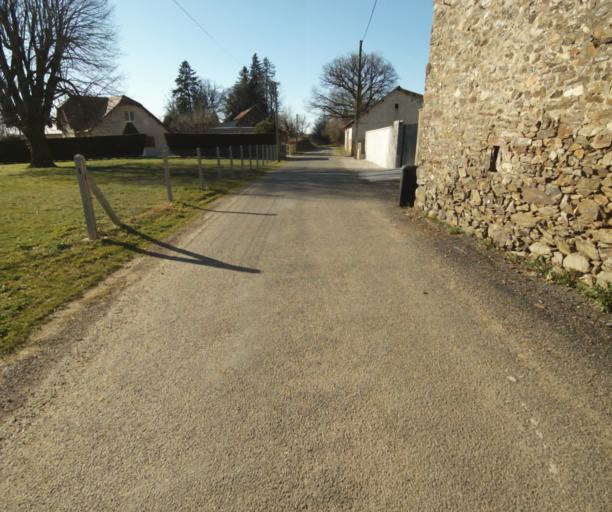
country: FR
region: Limousin
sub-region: Departement de la Correze
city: Seilhac
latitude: 45.3791
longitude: 1.7134
